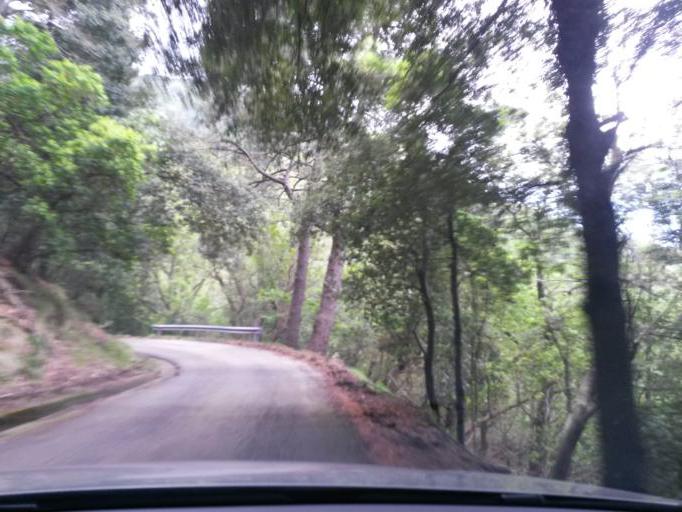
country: IT
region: Tuscany
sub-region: Provincia di Livorno
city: Marciana
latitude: 42.7771
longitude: 10.1846
